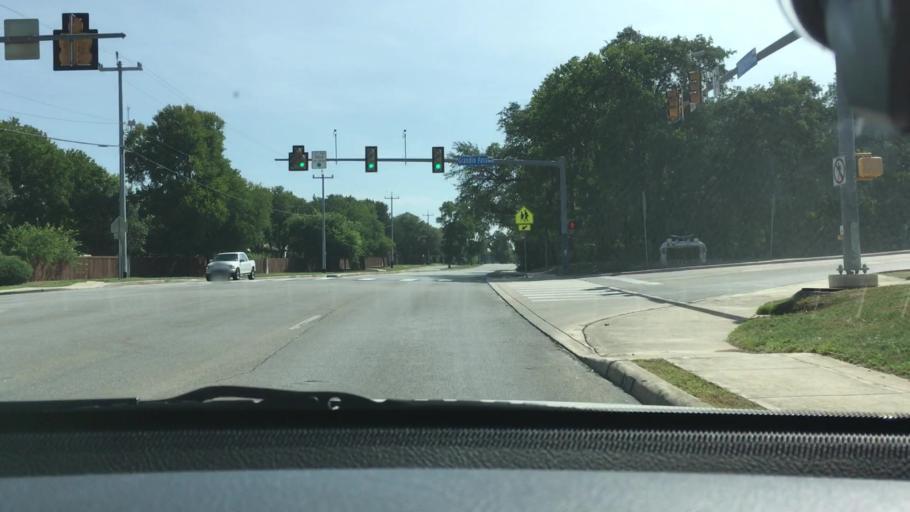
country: US
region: Texas
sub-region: Bexar County
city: Live Oak
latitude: 29.5948
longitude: -98.3900
